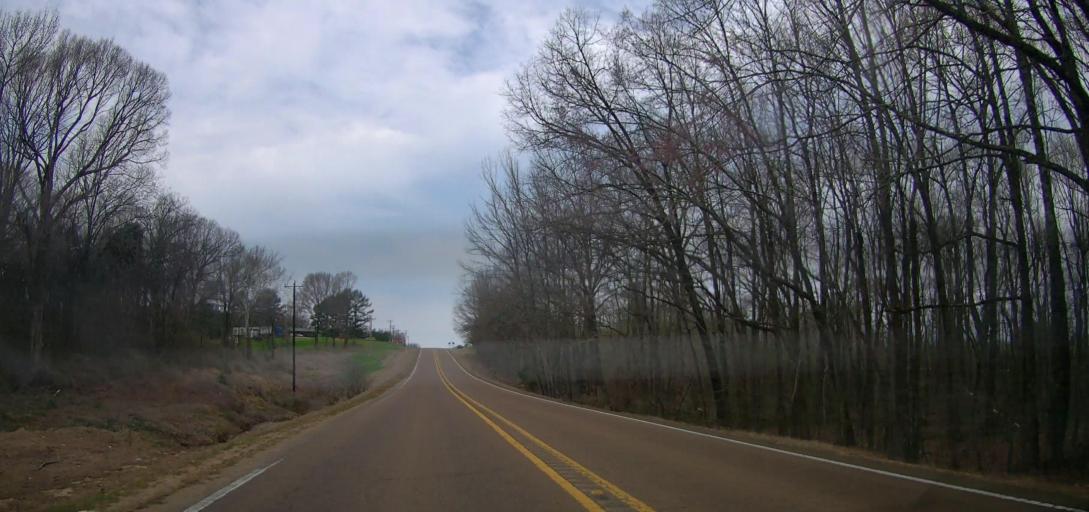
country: US
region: Mississippi
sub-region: Marshall County
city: Byhalia
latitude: 34.8592
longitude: -89.6510
